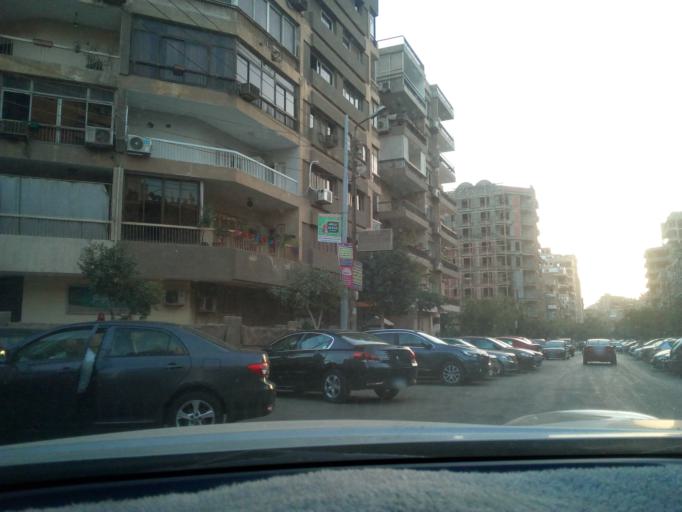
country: EG
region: Muhafazat al Qahirah
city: Cairo
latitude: 30.0869
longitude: 31.3456
